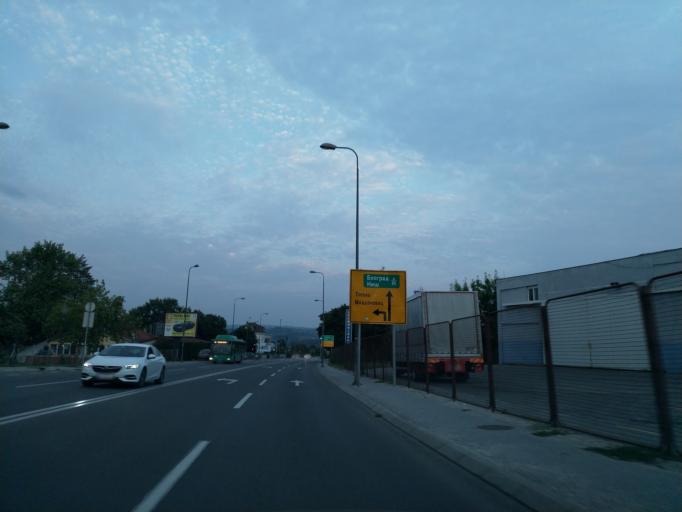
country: RS
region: Central Serbia
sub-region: Sumadijski Okrug
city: Kragujevac
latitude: 44.0300
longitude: 20.9149
